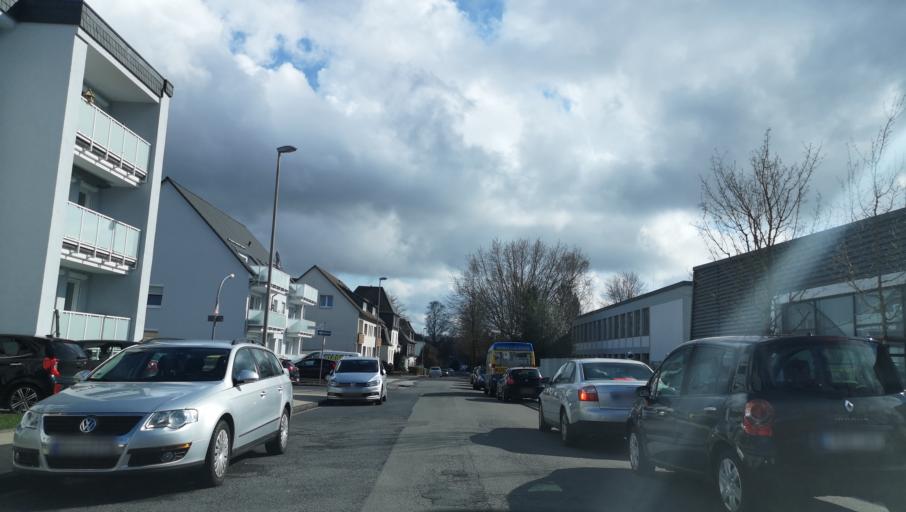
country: DE
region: North Rhine-Westphalia
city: Wermelskirchen
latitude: 51.1947
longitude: 7.2687
